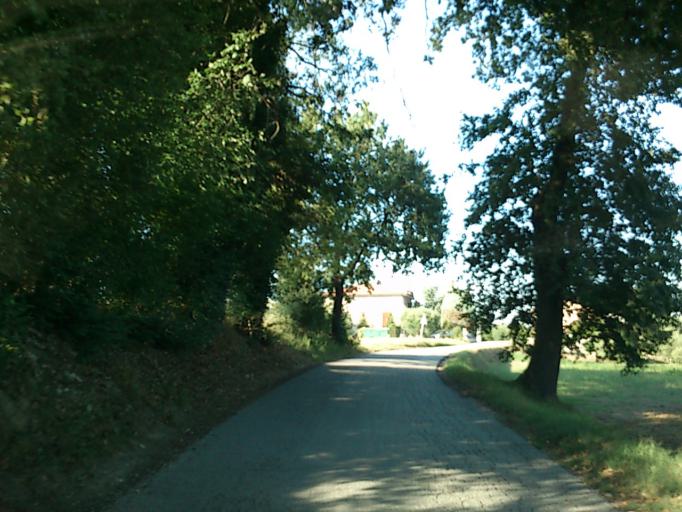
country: IT
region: The Marches
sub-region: Provincia di Pesaro e Urbino
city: Saltara
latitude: 43.7391
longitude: 12.9076
